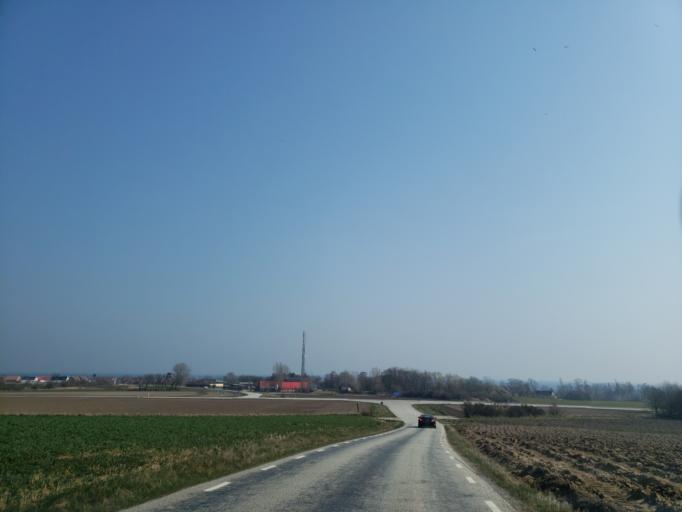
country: SE
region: Skane
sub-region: Simrishamns Kommun
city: Simrishamn
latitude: 55.5109
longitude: 14.3326
